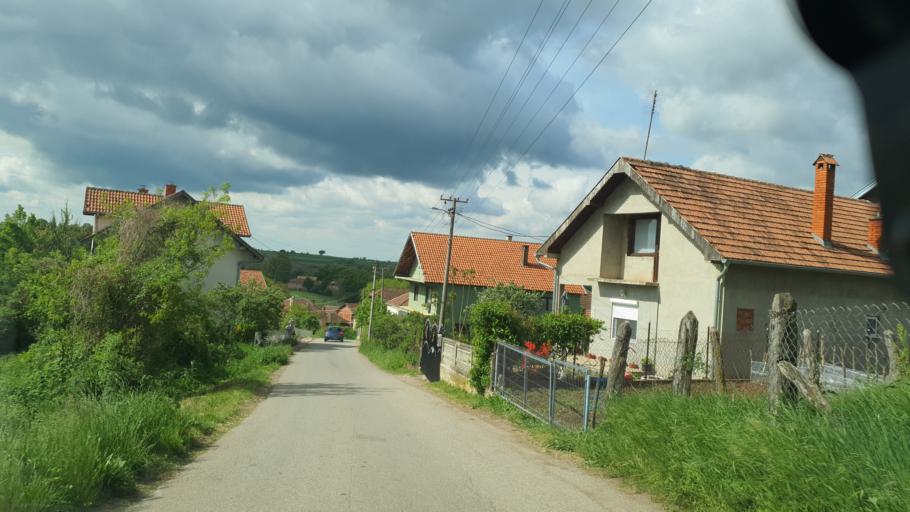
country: RS
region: Central Serbia
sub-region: Pomoravski Okrug
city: Paracin
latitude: 43.9385
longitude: 21.4938
